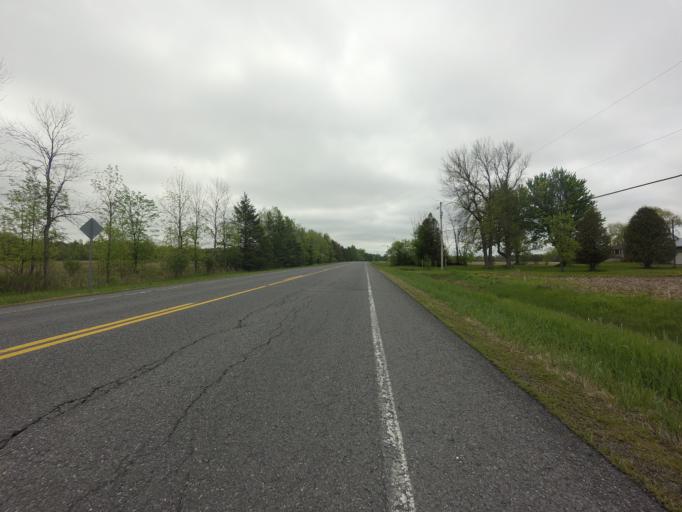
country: CA
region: Ontario
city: Casselman
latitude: 45.0565
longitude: -75.2024
